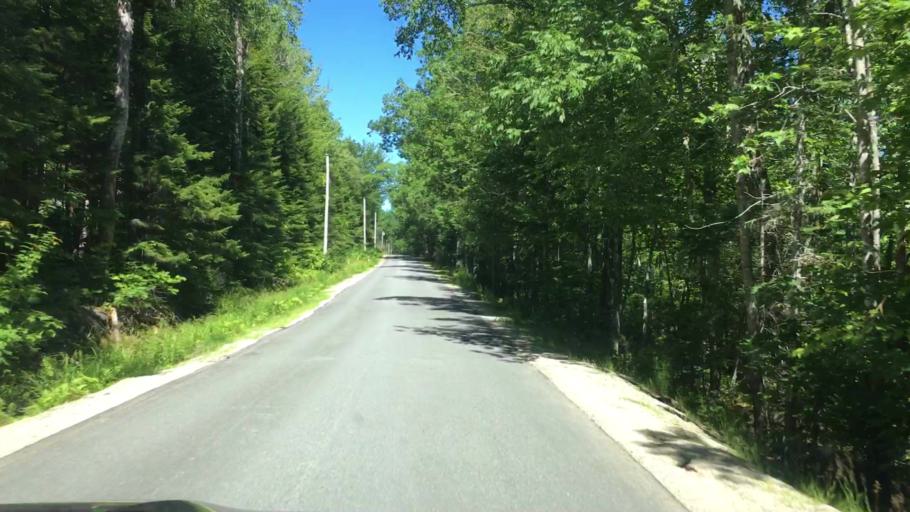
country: US
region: Maine
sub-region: Hancock County
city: Sedgwick
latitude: 44.3372
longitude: -68.6630
